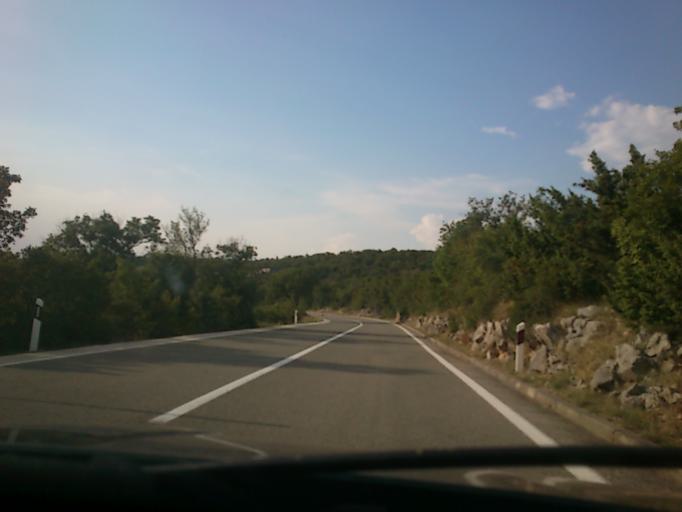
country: HR
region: Primorsko-Goranska
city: Banjol
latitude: 44.7603
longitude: 14.9035
